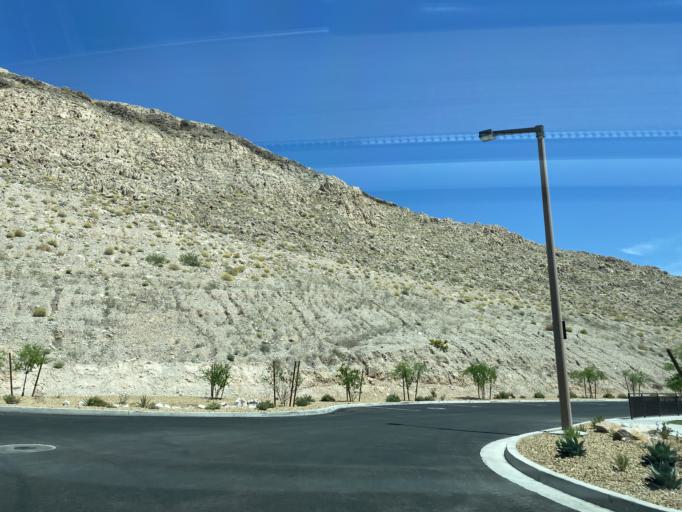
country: US
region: Nevada
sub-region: Clark County
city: Summerlin South
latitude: 36.2168
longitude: -115.3341
